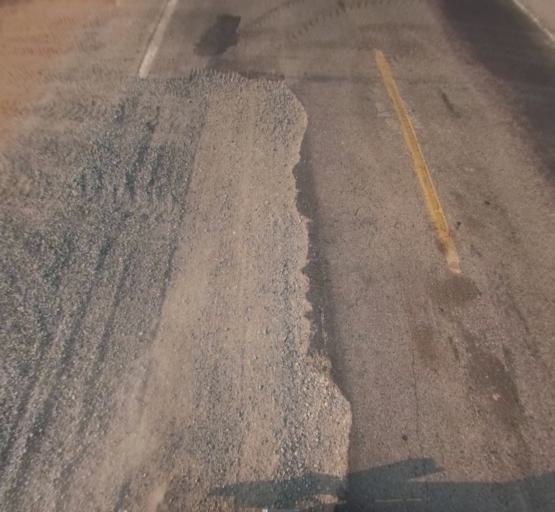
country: US
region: California
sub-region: Madera County
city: Madera Acres
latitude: 37.0508
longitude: -120.0561
